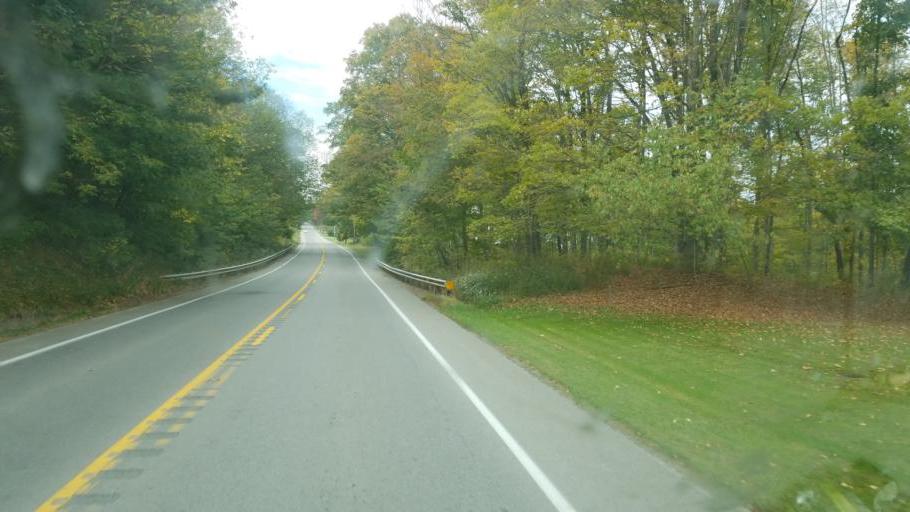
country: US
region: Pennsylvania
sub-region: Mercer County
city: Greenville
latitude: 41.4201
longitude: -80.3134
